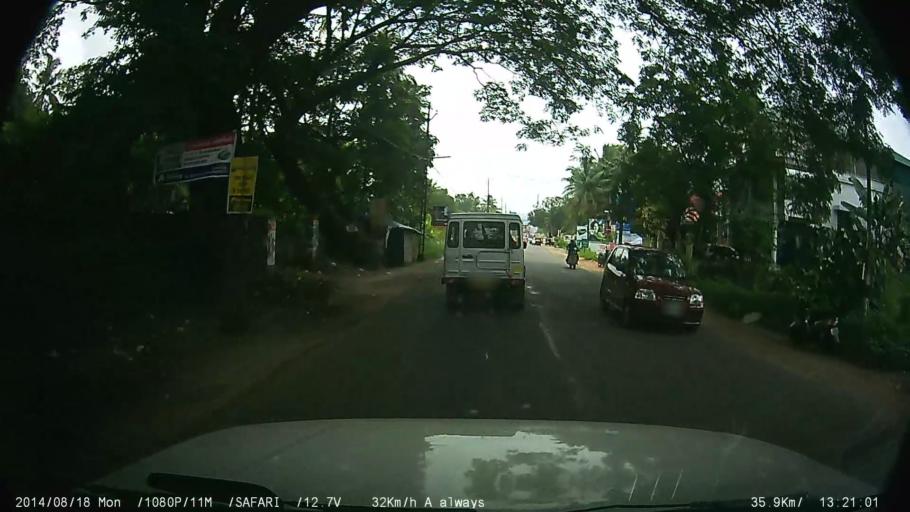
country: IN
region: Kerala
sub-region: Kottayam
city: Kottayam
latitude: 9.6147
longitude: 76.5323
